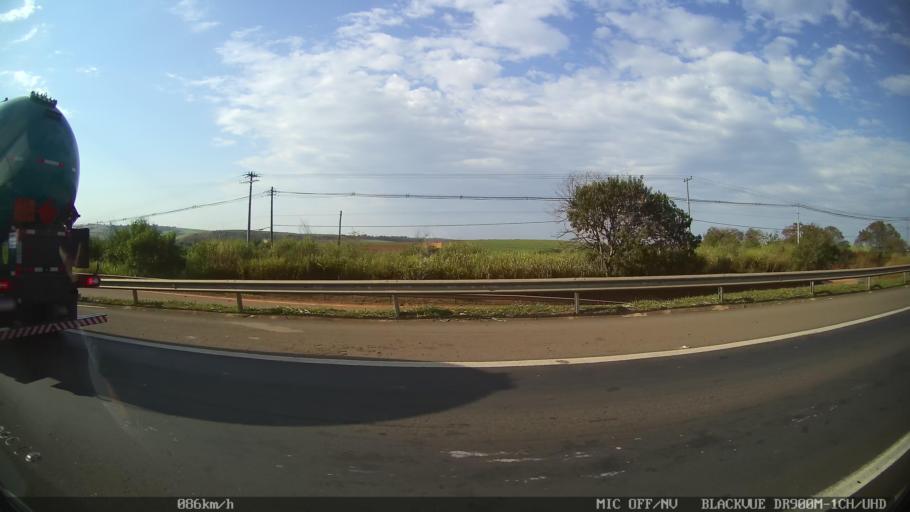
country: BR
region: Sao Paulo
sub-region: Cosmopolis
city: Cosmopolis
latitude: -22.6616
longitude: -47.1685
